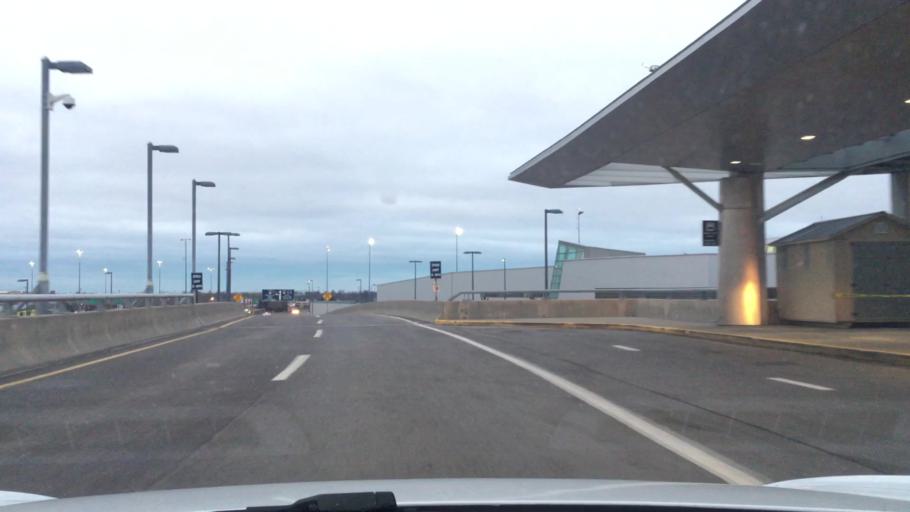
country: US
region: New York
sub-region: Erie County
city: Williamsville
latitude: 42.9336
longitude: -78.7324
